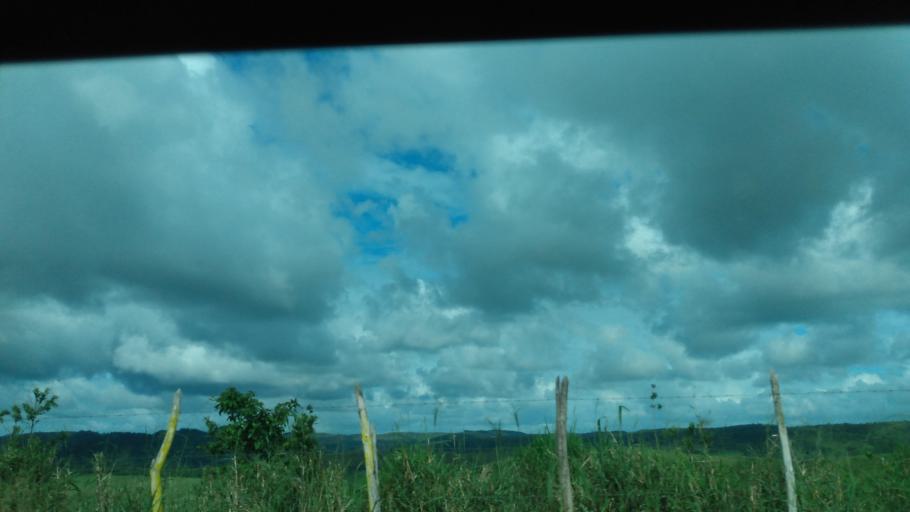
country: BR
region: Pernambuco
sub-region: Maraial
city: Maraial
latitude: -8.7896
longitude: -35.8805
